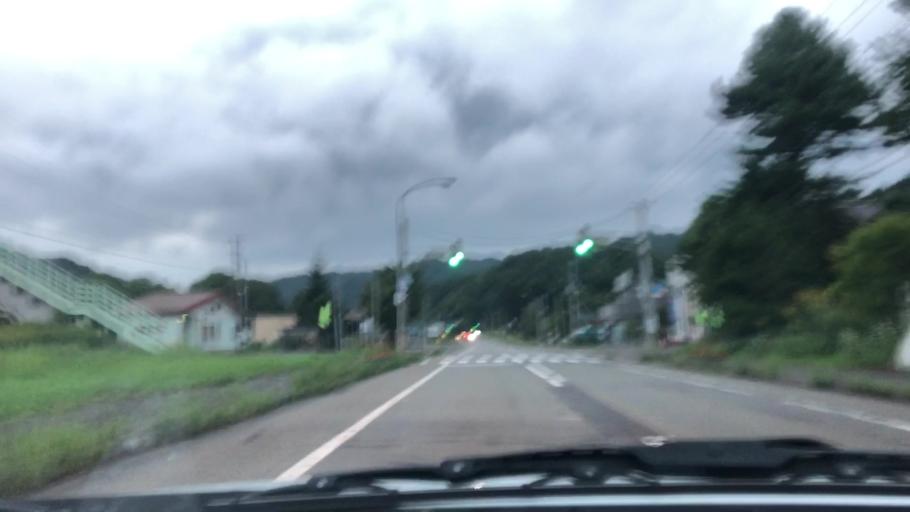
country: JP
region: Hokkaido
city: Chitose
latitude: 42.9102
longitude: 141.9771
